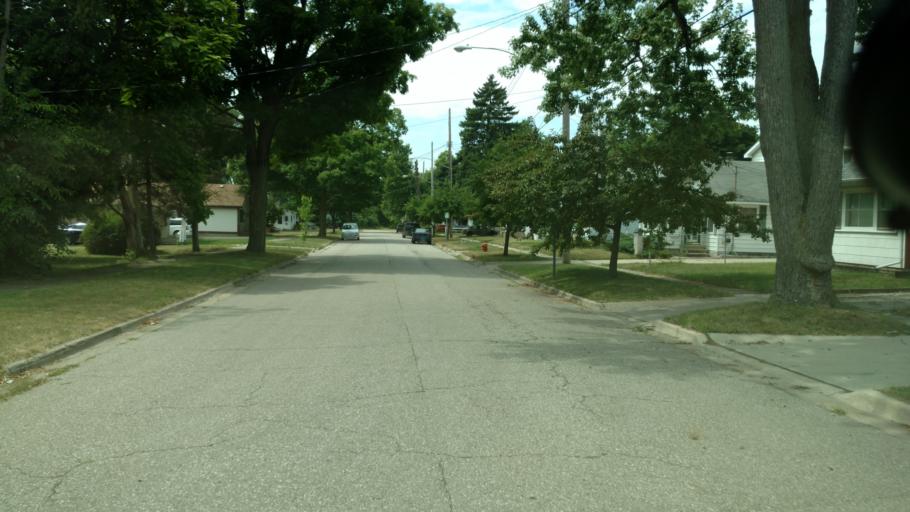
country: US
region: Michigan
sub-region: Ingham County
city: Lansing
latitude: 42.7588
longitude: -84.5554
